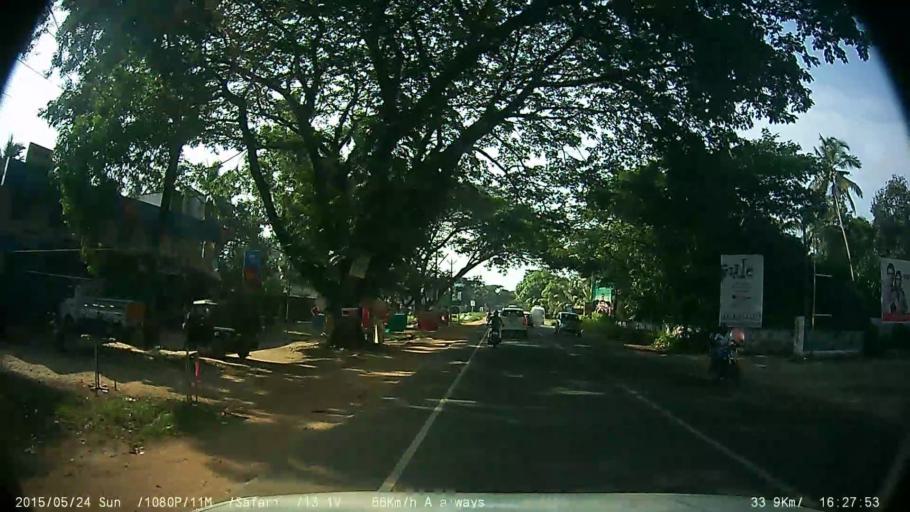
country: IN
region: Kerala
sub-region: Alappuzha
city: Alleppey
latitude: 9.5331
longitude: 76.3273
